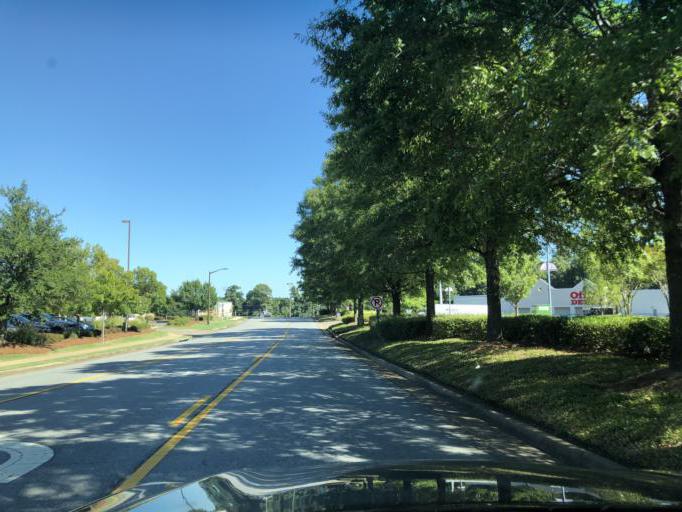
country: US
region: Alabama
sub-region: Russell County
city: Phenix City
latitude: 32.5177
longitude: -84.9549
